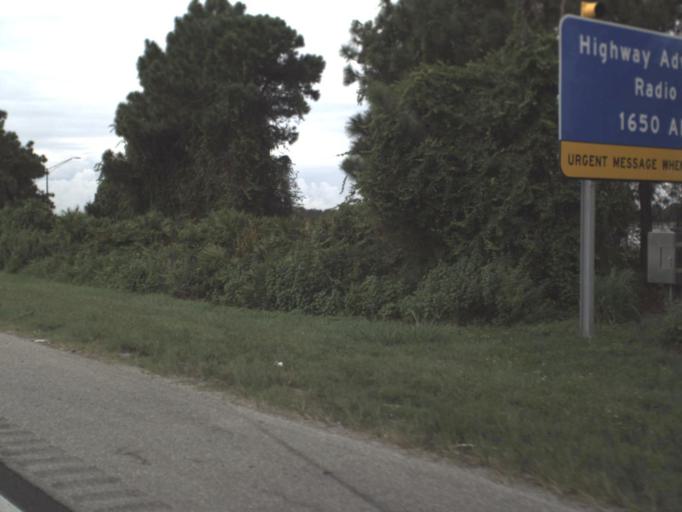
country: US
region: Florida
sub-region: Sarasota County
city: The Meadows
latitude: 27.3714
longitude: -82.4469
